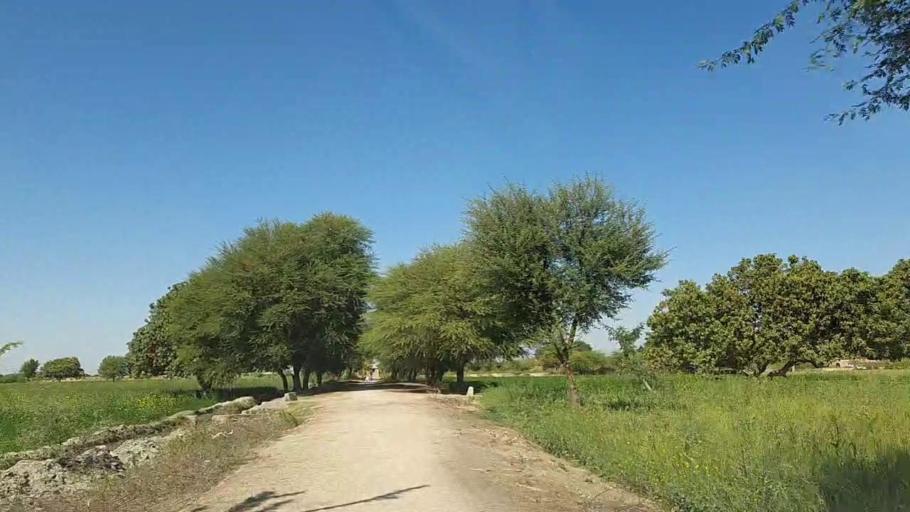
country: PK
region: Sindh
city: Samaro
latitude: 25.3042
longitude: 69.4649
